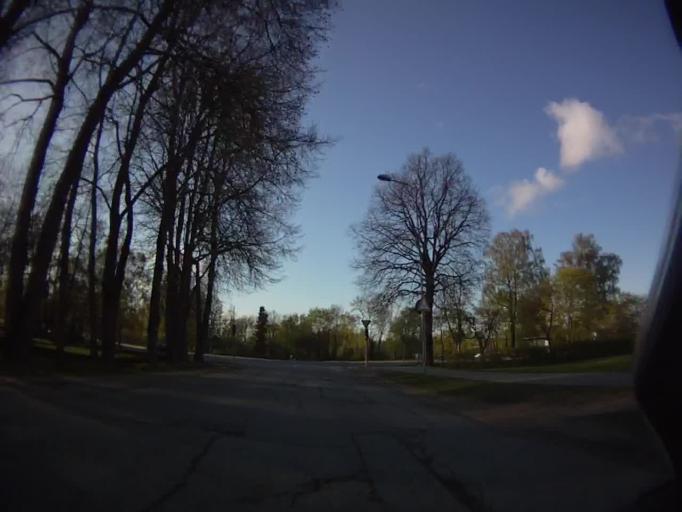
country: LV
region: Sigulda
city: Sigulda
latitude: 57.1519
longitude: 24.8904
